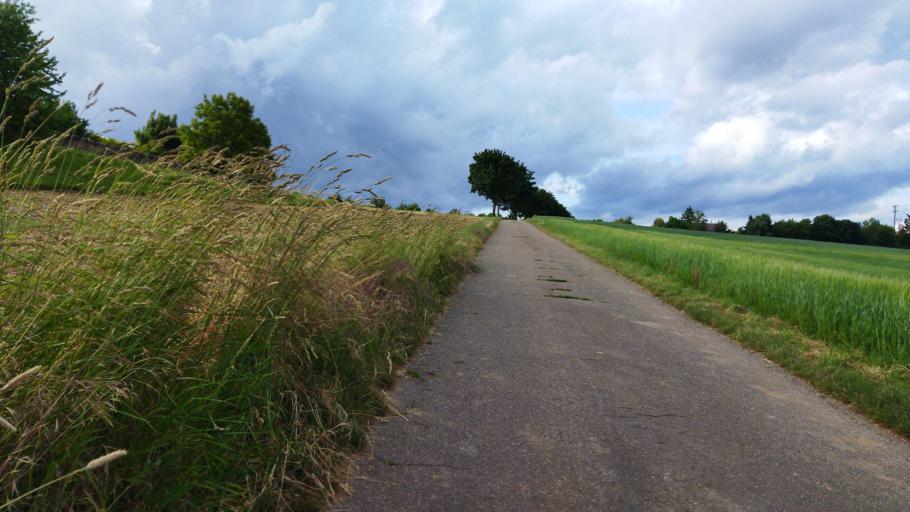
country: DE
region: Baden-Wuerttemberg
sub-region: Regierungsbezirk Stuttgart
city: Leingarten
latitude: 49.1773
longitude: 9.1290
